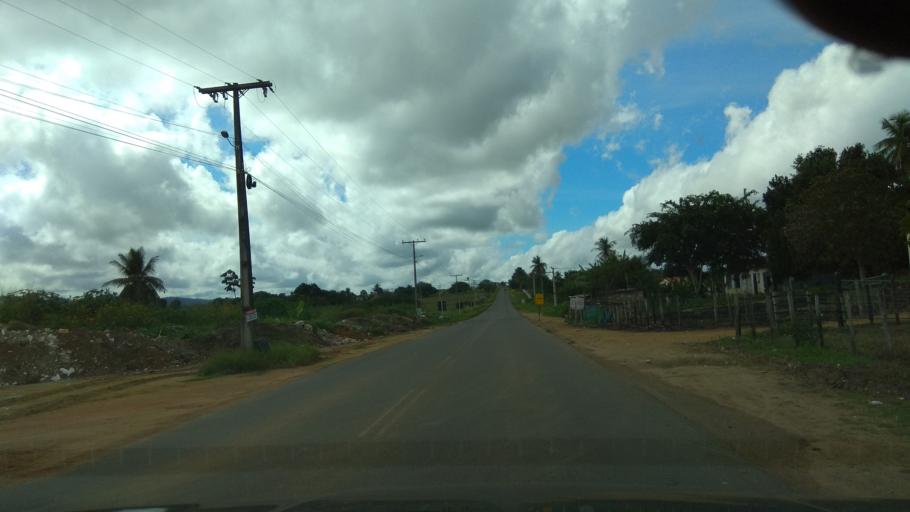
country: BR
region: Bahia
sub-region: Mutuipe
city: Mutuipe
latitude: -13.1653
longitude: -39.4061
